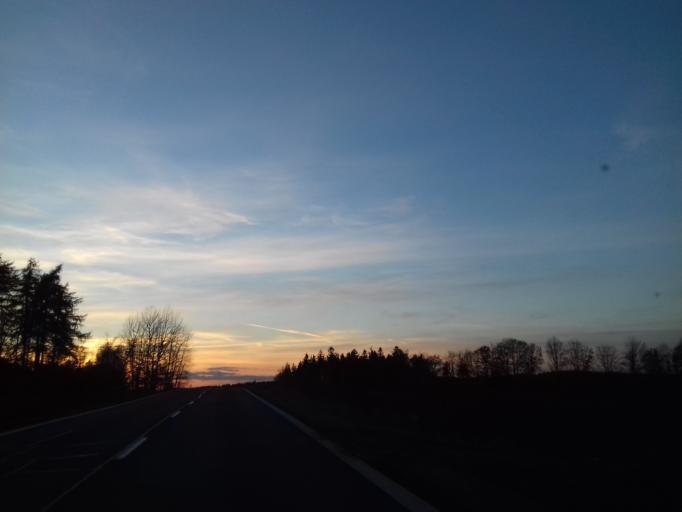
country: CZ
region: Vysocina
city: Krizova
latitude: 49.6763
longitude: 15.7688
